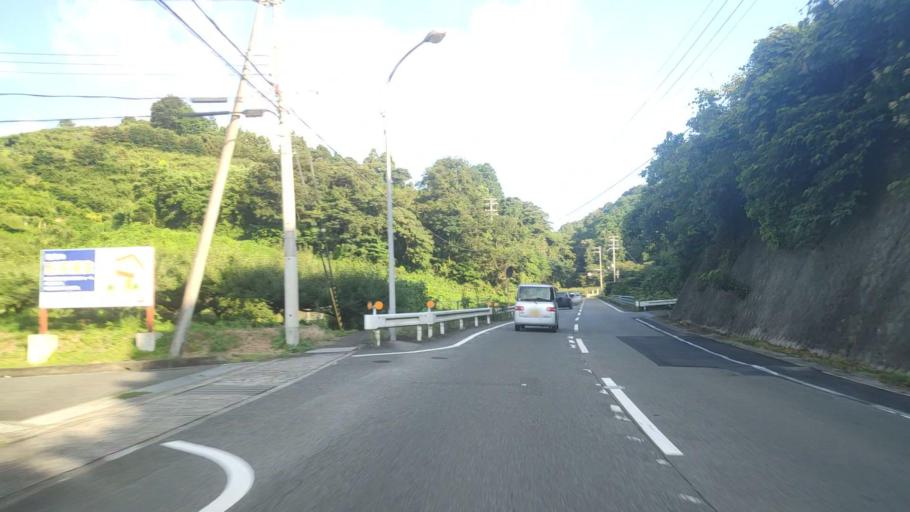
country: JP
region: Wakayama
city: Tanabe
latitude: 33.7335
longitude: 135.4324
